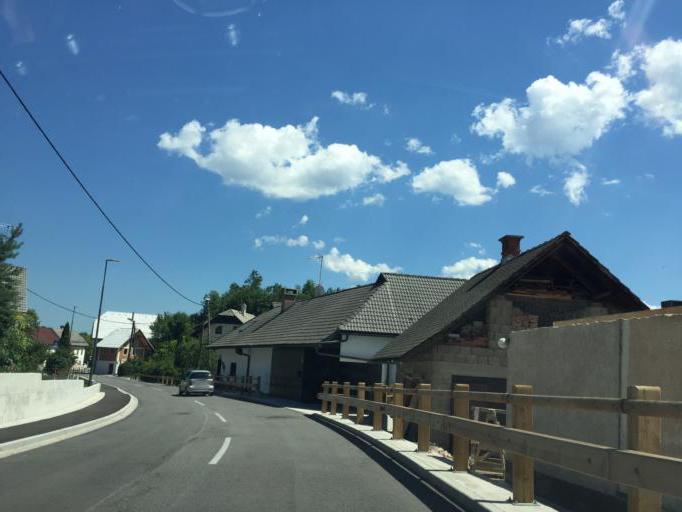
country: SI
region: Gorje
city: Zgornje Gorje
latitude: 46.3774
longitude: 14.0880
